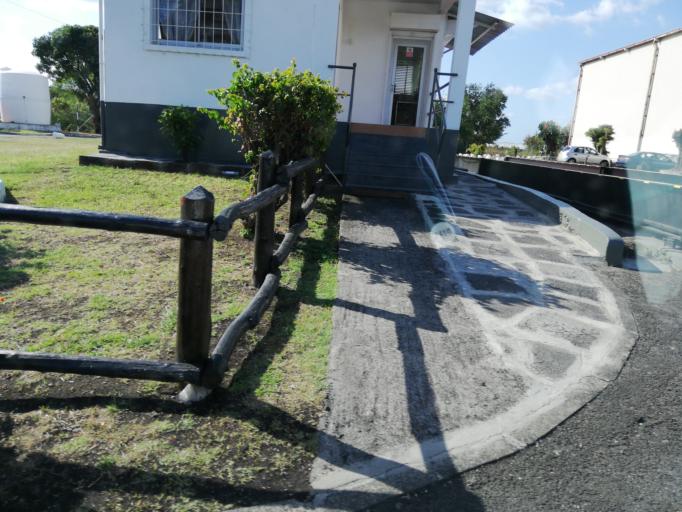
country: MU
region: Port Louis
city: Port Louis
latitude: -20.1609
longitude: 57.4926
